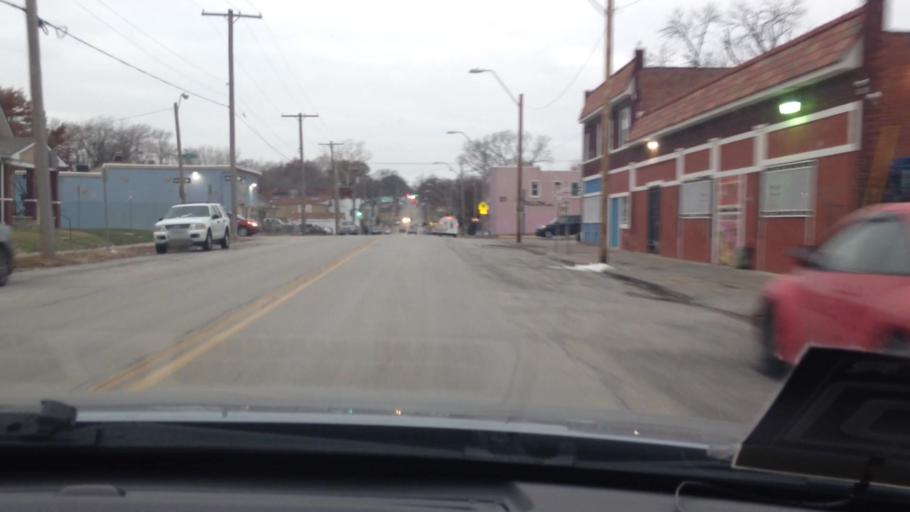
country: US
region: Missouri
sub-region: Clay County
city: North Kansas City
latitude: 39.1123
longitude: -94.5122
